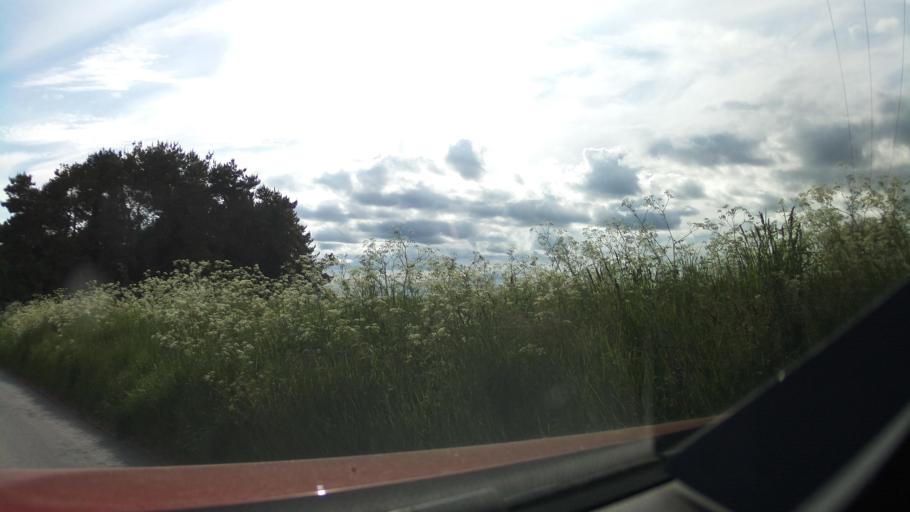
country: GB
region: England
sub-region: Gloucestershire
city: Donnington
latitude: 51.9600
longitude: -1.7636
